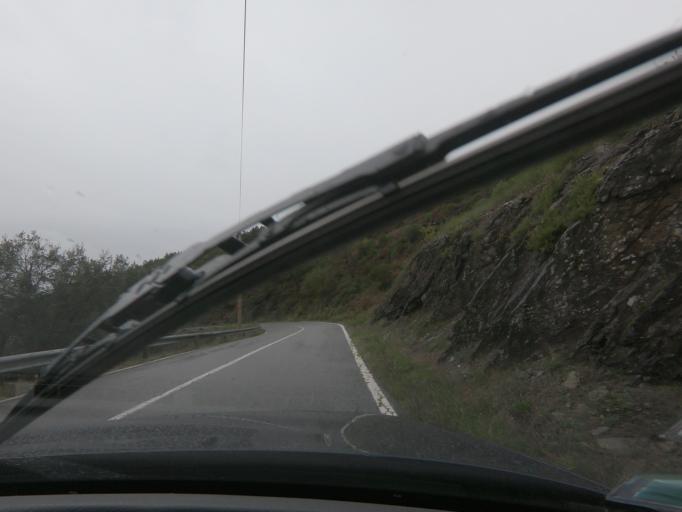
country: PT
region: Vila Real
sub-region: Mondim de Basto
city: Mondim de Basto
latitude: 41.3506
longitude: -7.9012
